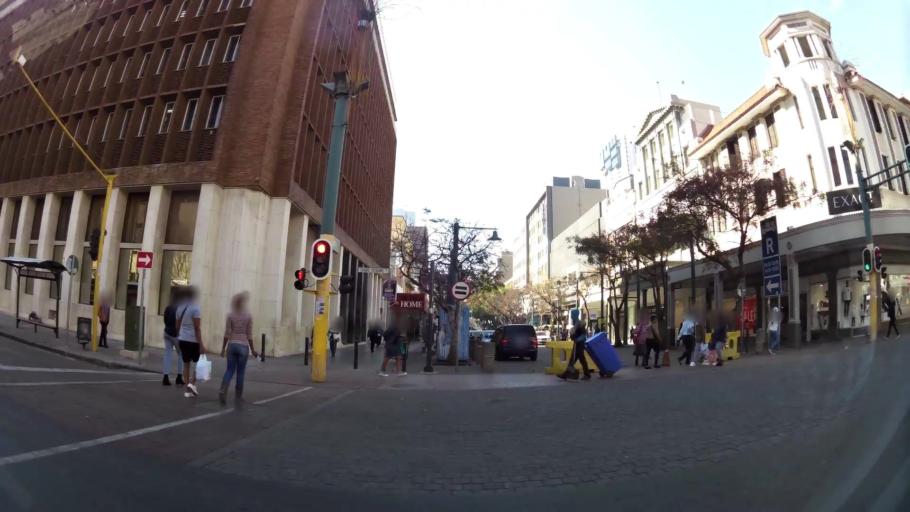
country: ZA
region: Gauteng
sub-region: City of Tshwane Metropolitan Municipality
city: Pretoria
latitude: -25.7464
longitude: 28.1906
